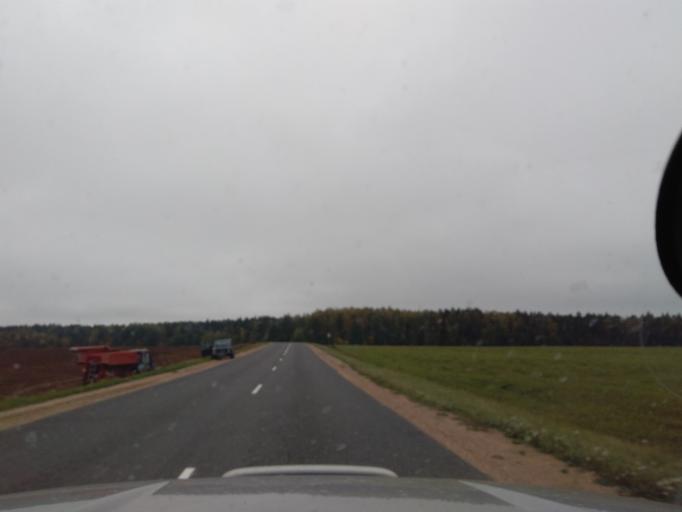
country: BY
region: Minsk
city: Kapyl'
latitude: 53.1553
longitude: 27.2313
